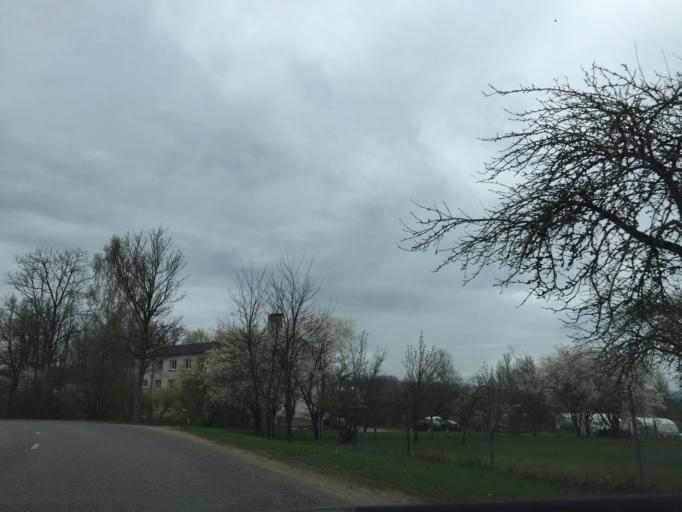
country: LV
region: Sigulda
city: Sigulda
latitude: 57.0268
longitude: 24.8173
